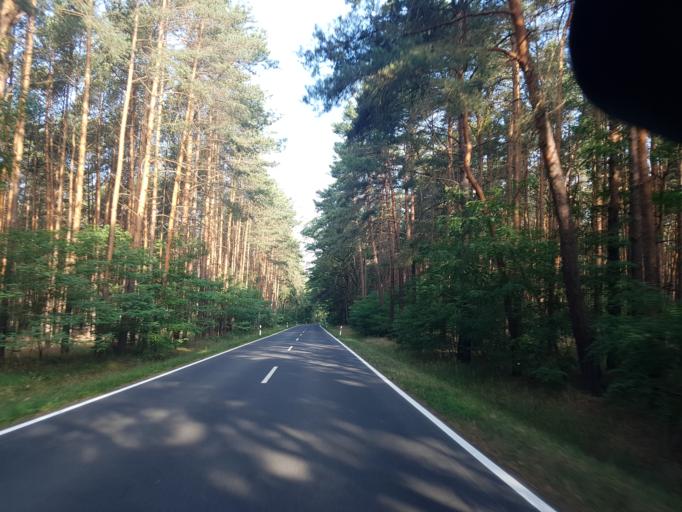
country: DE
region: Saxony-Anhalt
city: Holzdorf
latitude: 51.8500
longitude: 13.1288
